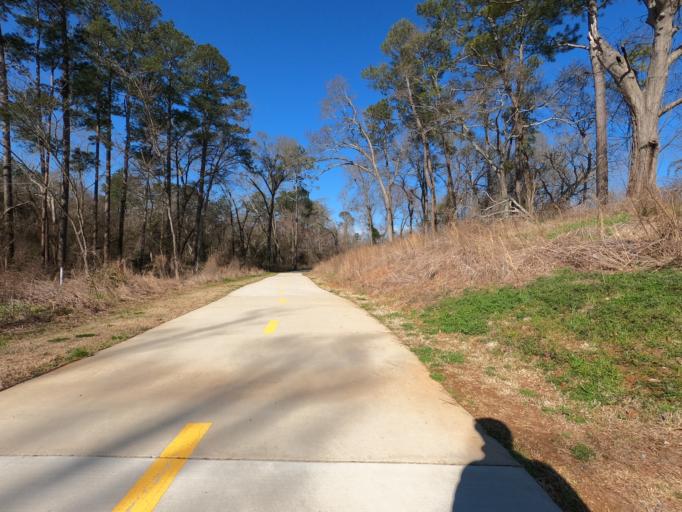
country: US
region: Georgia
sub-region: Clarke County
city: Athens
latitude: 33.9682
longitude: -83.3745
